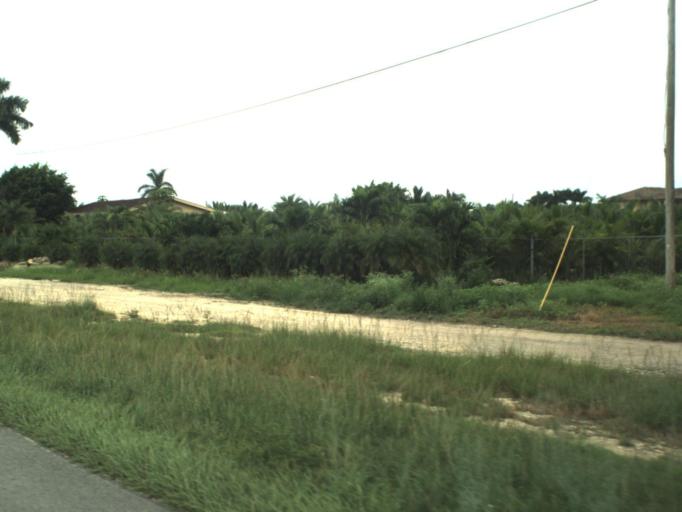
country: US
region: Florida
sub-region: Miami-Dade County
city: The Hammocks
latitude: 25.6689
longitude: -80.4812
